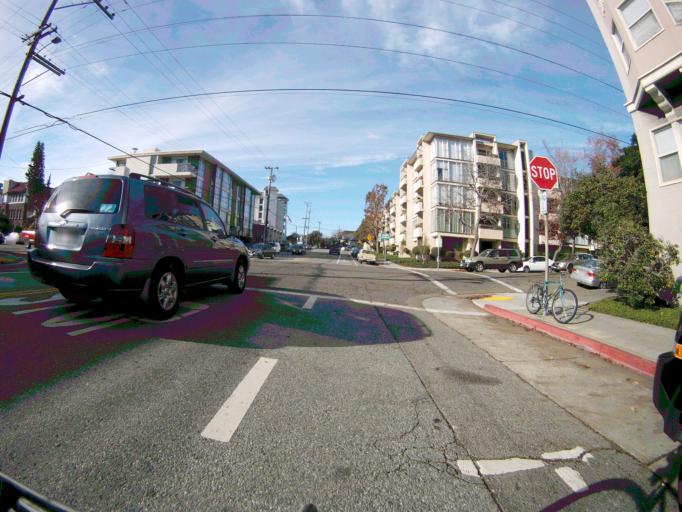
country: US
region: California
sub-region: Alameda County
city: Piedmont
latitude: 37.8270
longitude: -122.2531
